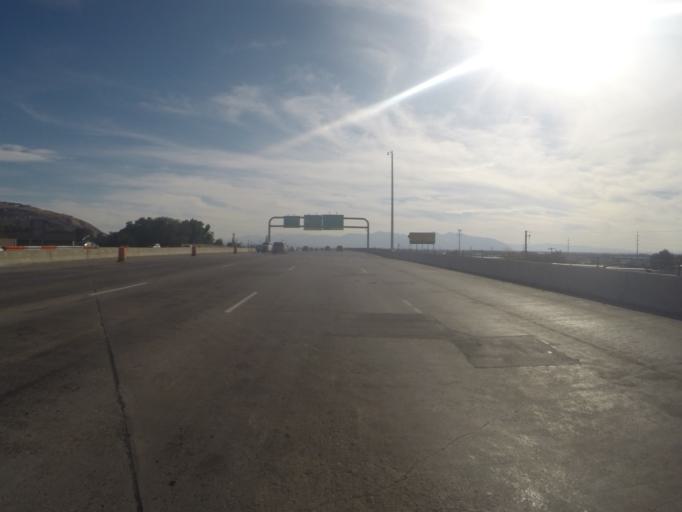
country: US
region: Utah
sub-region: Davis County
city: North Salt Lake
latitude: 40.8511
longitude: -111.9116
